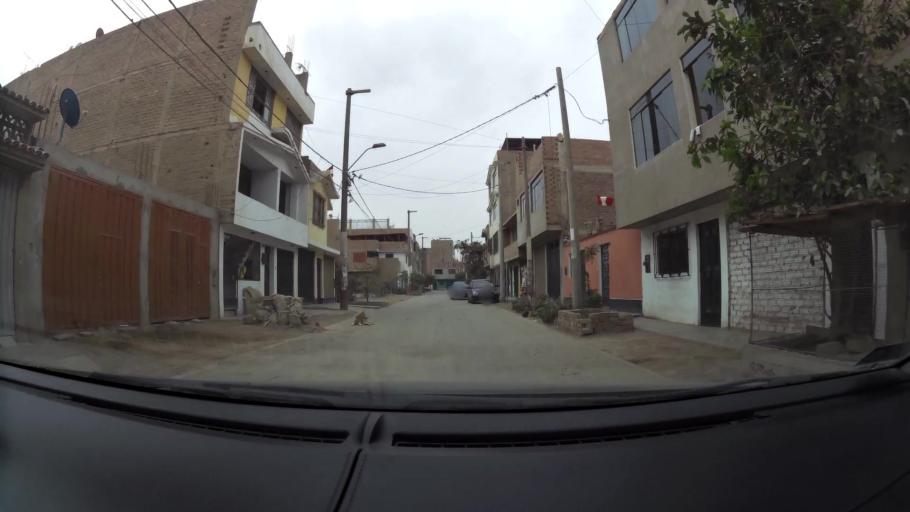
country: PE
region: Lima
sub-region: Lima
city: Independencia
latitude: -11.9680
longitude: -77.0919
